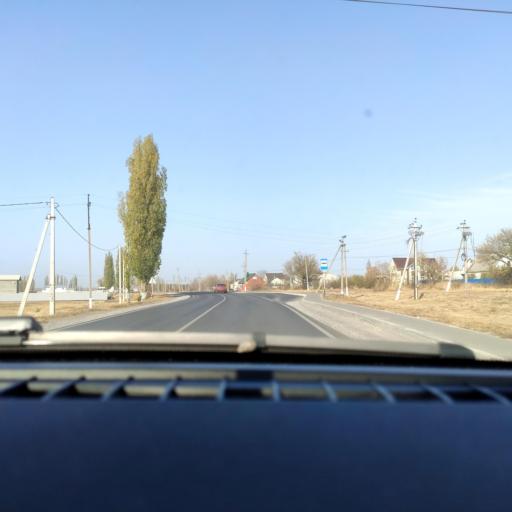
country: RU
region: Voronezj
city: Novaya Usman'
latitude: 51.6571
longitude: 39.4050
